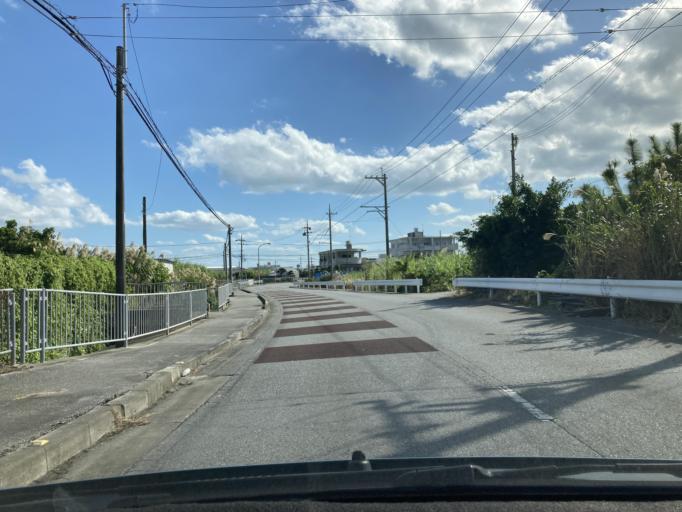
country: JP
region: Okinawa
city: Gushikawa
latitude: 26.3450
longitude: 127.8479
